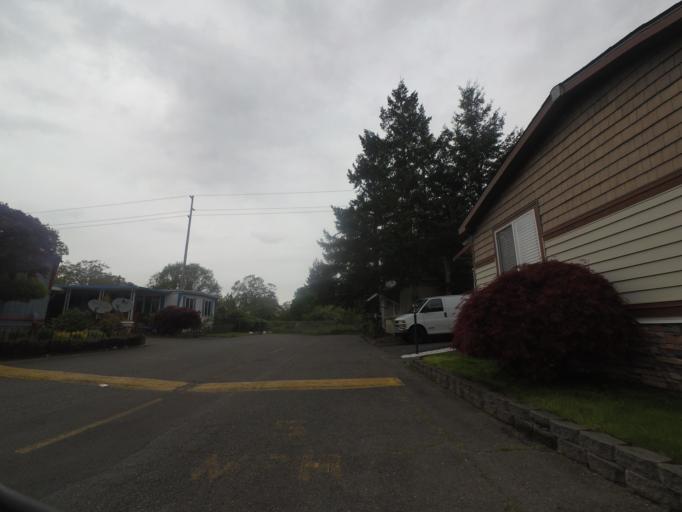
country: US
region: Washington
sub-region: Pierce County
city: Lakewood
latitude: 47.1845
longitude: -122.4789
